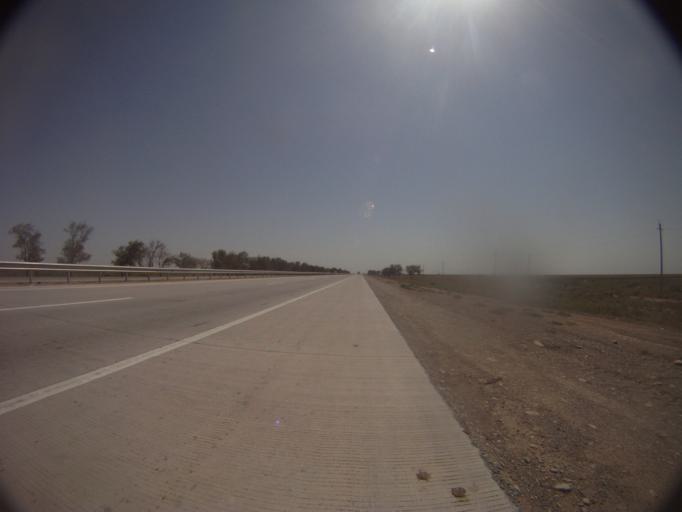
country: KZ
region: Ongtustik Qazaqstan
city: Bayaldyr
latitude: 43.0579
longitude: 68.6880
